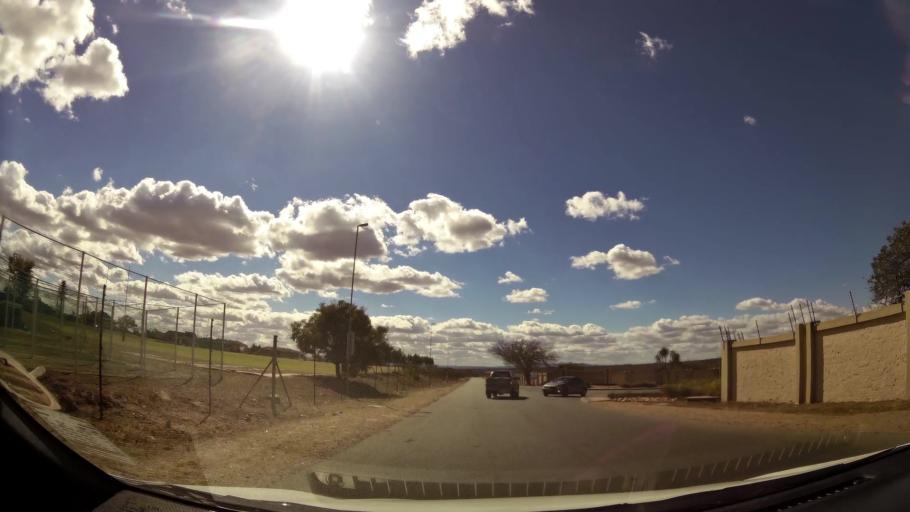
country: ZA
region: Limpopo
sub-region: Capricorn District Municipality
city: Polokwane
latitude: -23.8658
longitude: 29.5096
